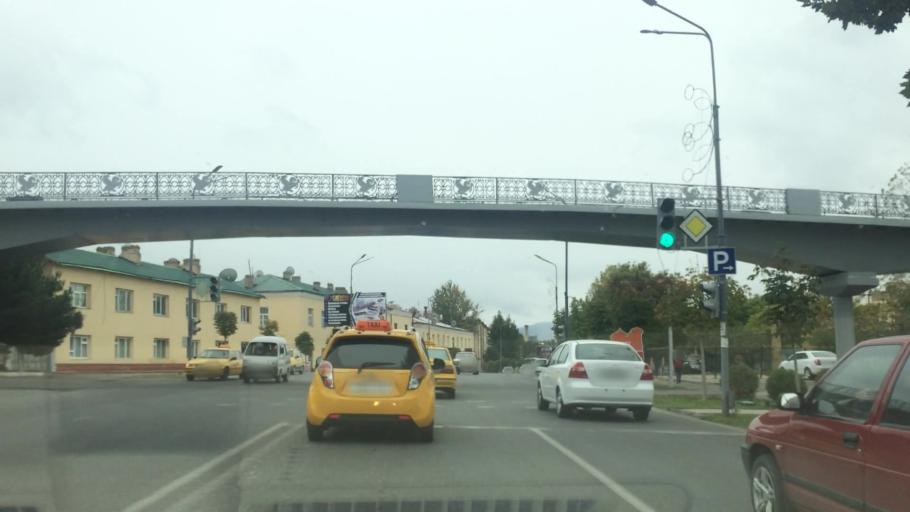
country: UZ
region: Samarqand
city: Samarqand
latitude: 39.6555
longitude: 66.9711
